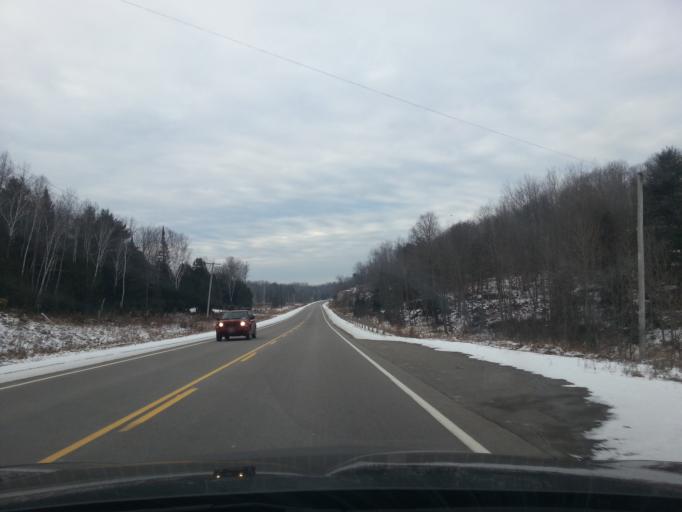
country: CA
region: Ontario
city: Skatepark
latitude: 44.7452
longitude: -76.9212
